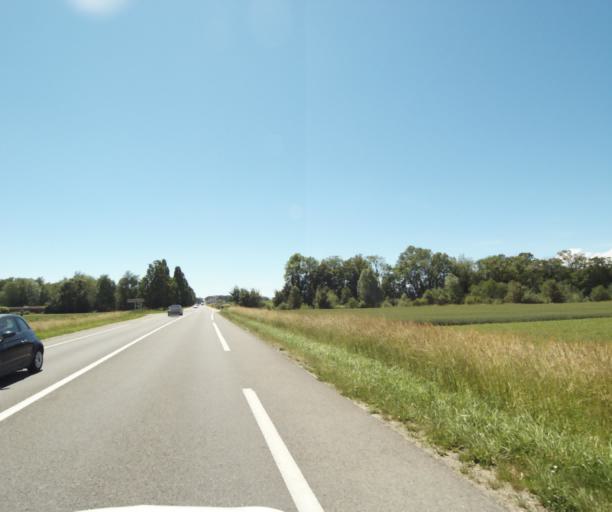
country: FR
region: Rhone-Alpes
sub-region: Departement de la Haute-Savoie
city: Veigy-Foncenex
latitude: 46.2736
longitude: 6.2435
